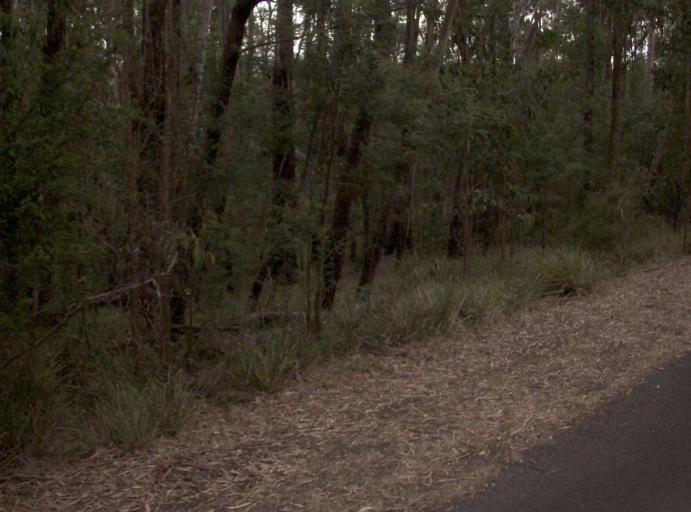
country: AU
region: Victoria
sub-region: Wellington
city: Sale
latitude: -38.4366
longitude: 146.9487
